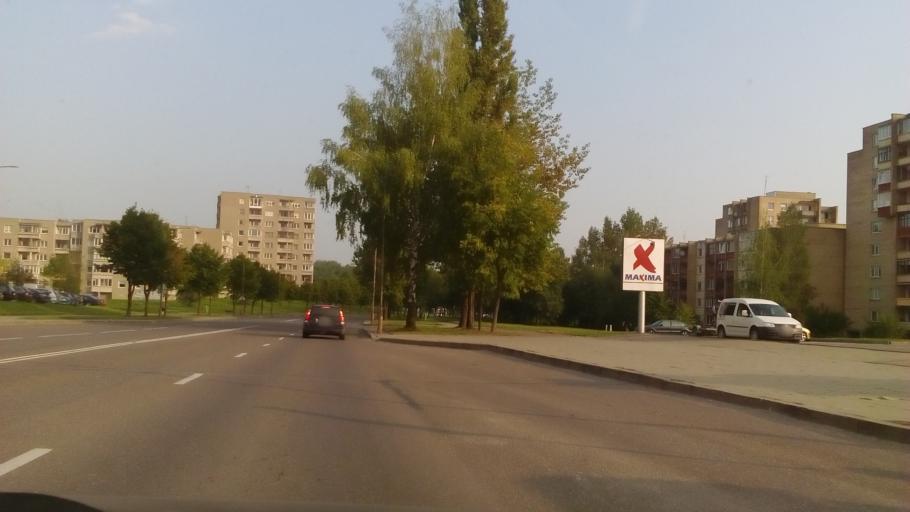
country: LT
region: Alytaus apskritis
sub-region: Alytus
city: Alytus
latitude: 54.3969
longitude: 24.0162
